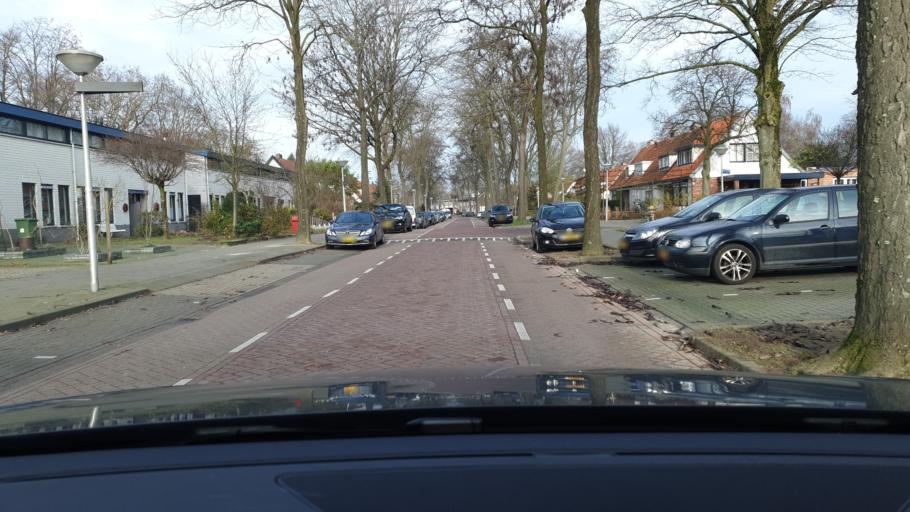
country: NL
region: North Brabant
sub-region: Gemeente Eindhoven
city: De Doornakkers
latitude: 51.4395
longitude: 5.5140
